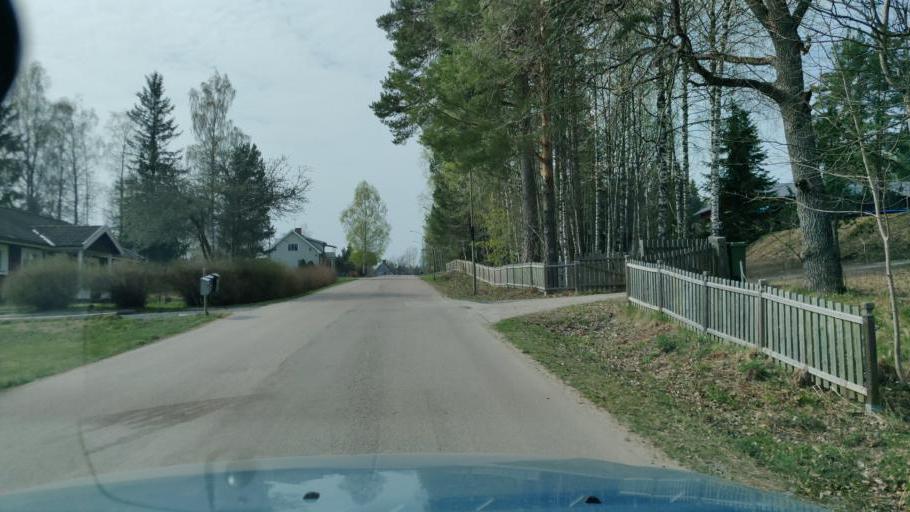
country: SE
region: Vaermland
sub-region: Munkfors Kommun
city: Munkfors
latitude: 59.8344
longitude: 13.5180
